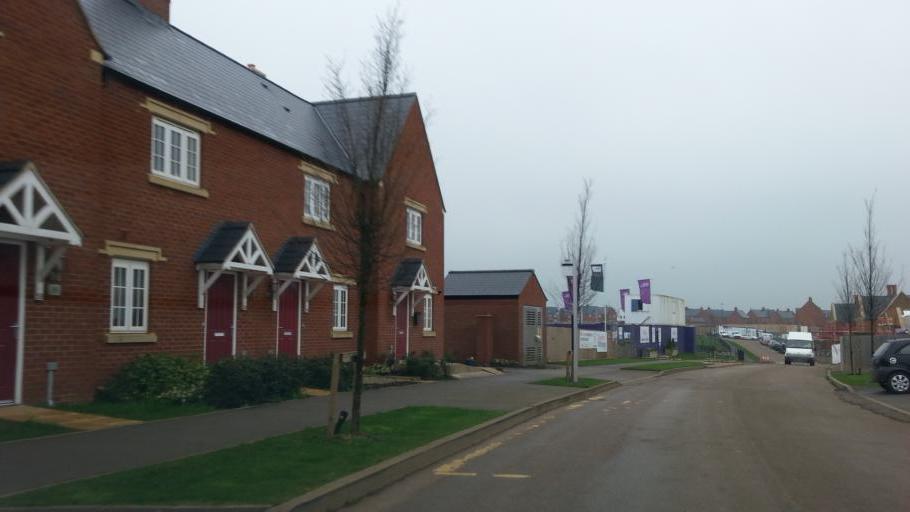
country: GB
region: England
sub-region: Northamptonshire
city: Brackley
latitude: 52.0434
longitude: -1.1472
